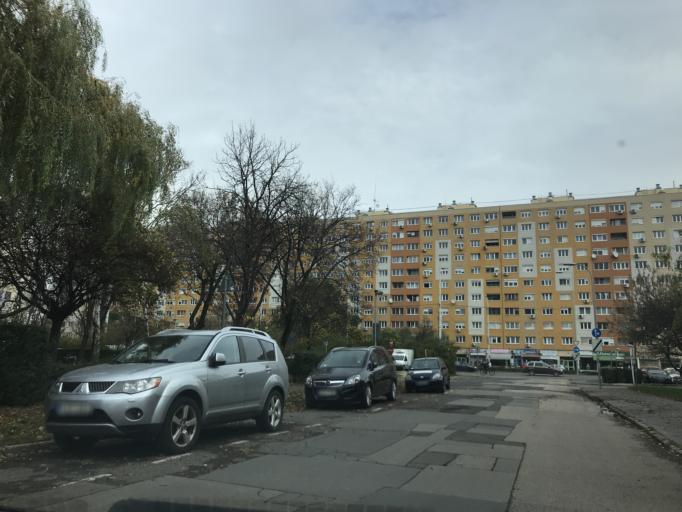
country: HU
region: Budapest
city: Budapest III. keruelet
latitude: 47.5434
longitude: 19.0354
